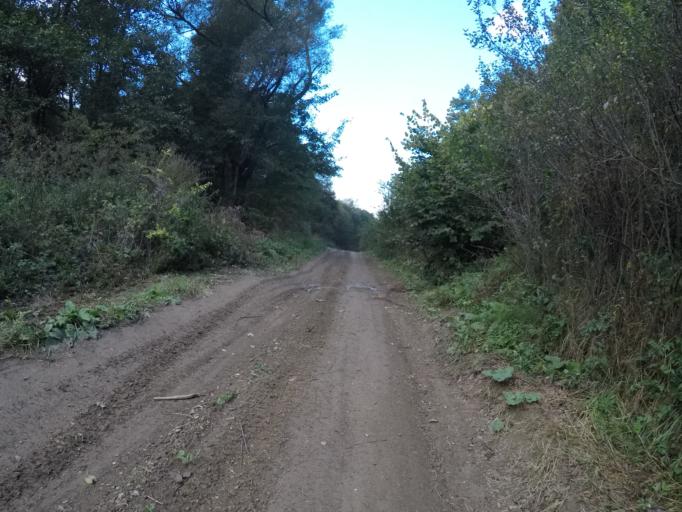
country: SK
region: Presovsky
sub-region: Okres Presov
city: Presov
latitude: 48.9307
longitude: 21.1684
